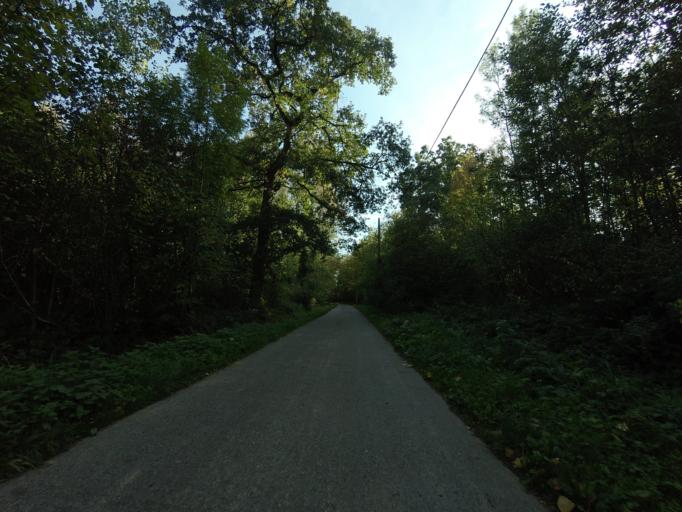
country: BE
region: Flanders
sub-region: Provincie Vlaams-Brabant
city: Kampenhout
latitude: 50.9157
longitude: 4.5959
